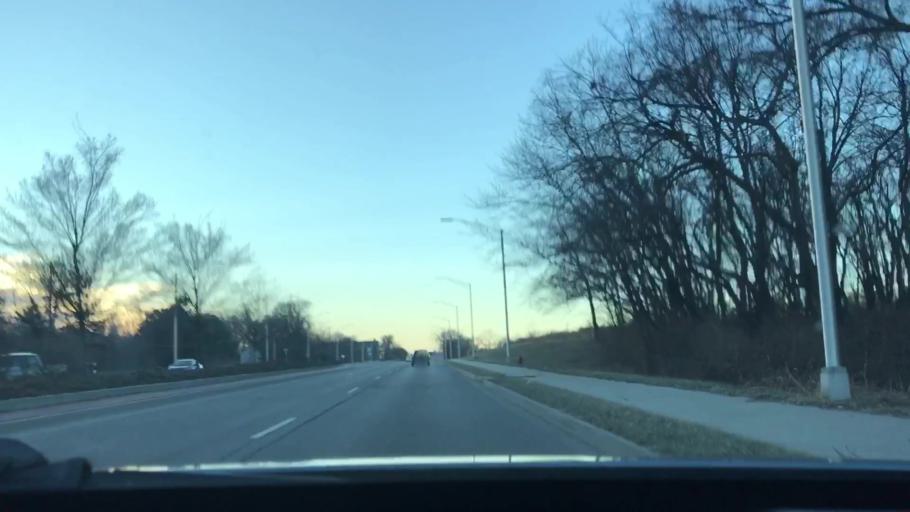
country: US
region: Kansas
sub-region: Wyandotte County
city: Edwardsville
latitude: 39.1164
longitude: -94.7905
